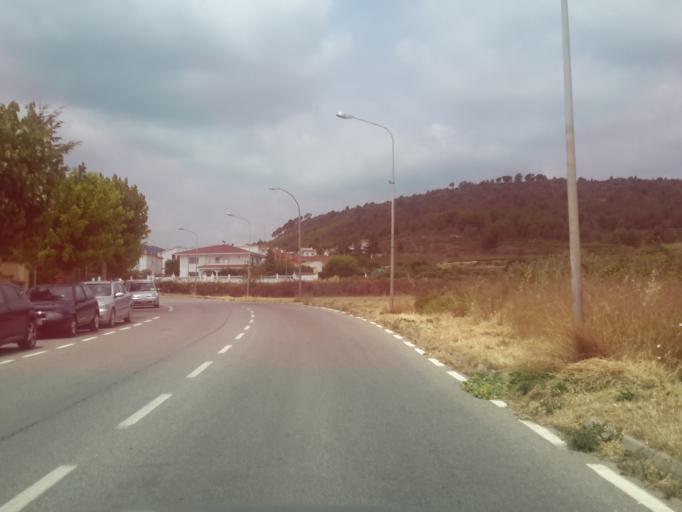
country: ES
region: Catalonia
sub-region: Provincia de Barcelona
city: Sant Marti Sarroca
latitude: 41.3894
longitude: 1.5692
